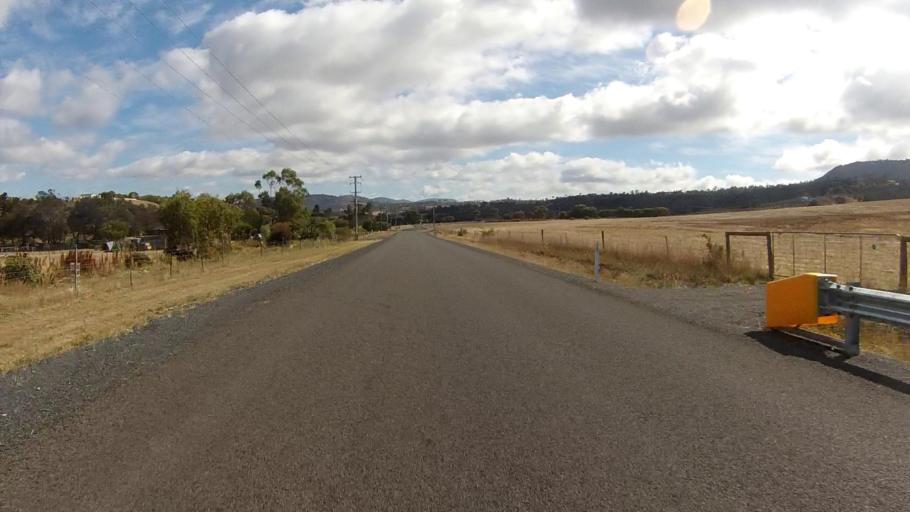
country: AU
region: Tasmania
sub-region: Brighton
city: Old Beach
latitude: -42.7628
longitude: 147.3006
